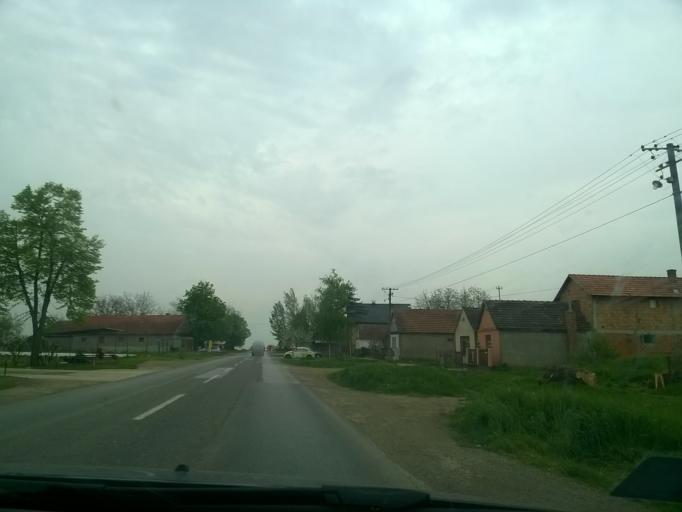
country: RS
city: Hrtkovci
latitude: 44.8697
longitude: 19.7704
